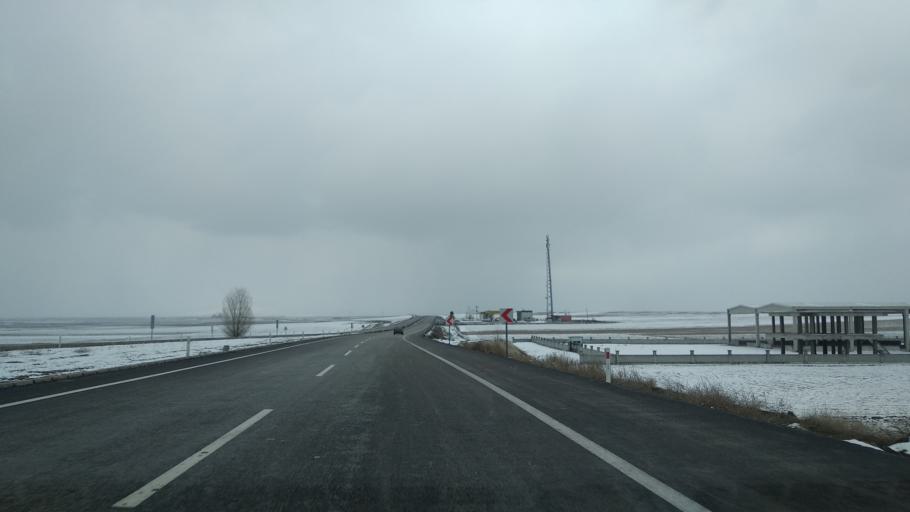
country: TR
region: Kayseri
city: Elbasi
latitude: 38.6514
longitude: 35.9945
